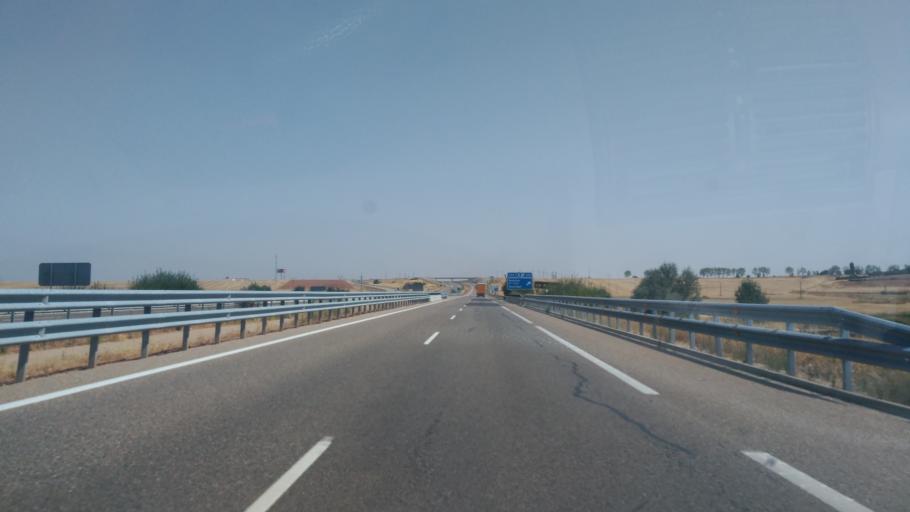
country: ES
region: Castille and Leon
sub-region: Provincia de Salamanca
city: Robliza de Cojos
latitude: 40.8705
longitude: -5.9939
